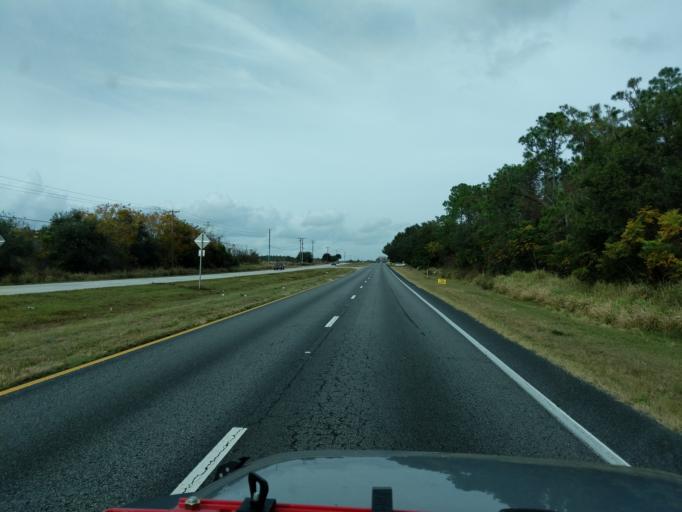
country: US
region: Florida
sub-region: Orange County
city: Zellwood
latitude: 28.7027
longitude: -81.5774
